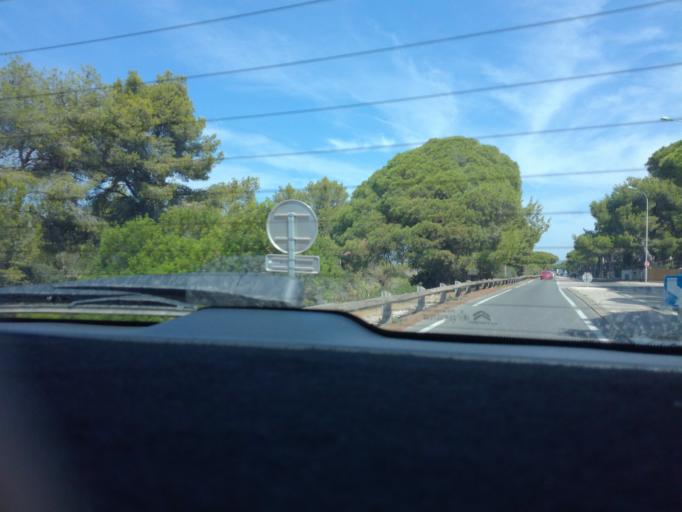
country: FR
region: Provence-Alpes-Cote d'Azur
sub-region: Departement du Var
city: Hyeres
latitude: 43.0748
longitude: 6.1486
